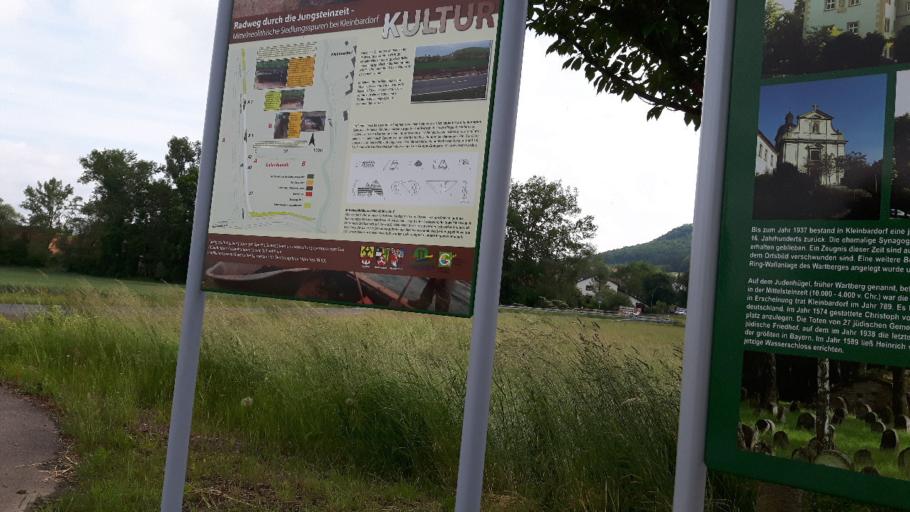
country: DE
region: Bavaria
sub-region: Regierungsbezirk Unterfranken
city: Sulzfeld
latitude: 50.2750
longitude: 10.3974
